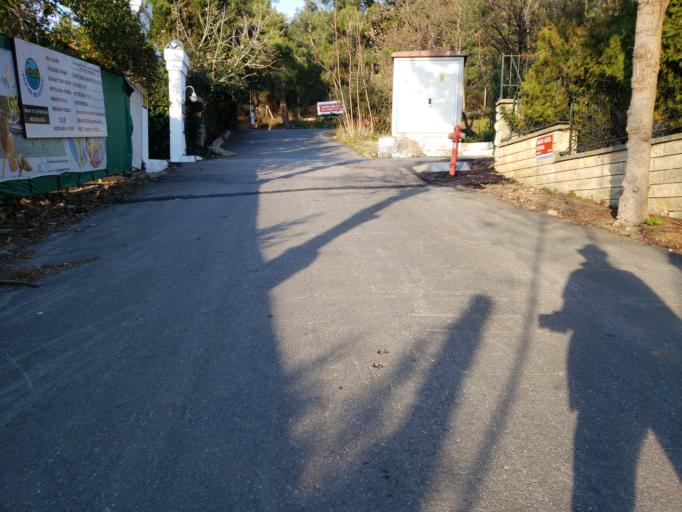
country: TR
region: Istanbul
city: Adalan
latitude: 40.8809
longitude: 29.0916
